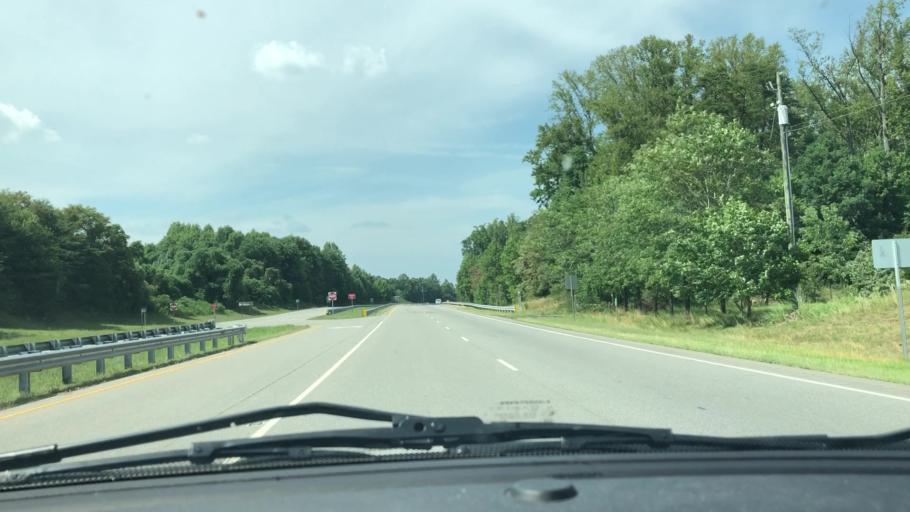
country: US
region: North Carolina
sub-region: Rockingham County
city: Stoneville
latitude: 36.5362
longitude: -79.9133
